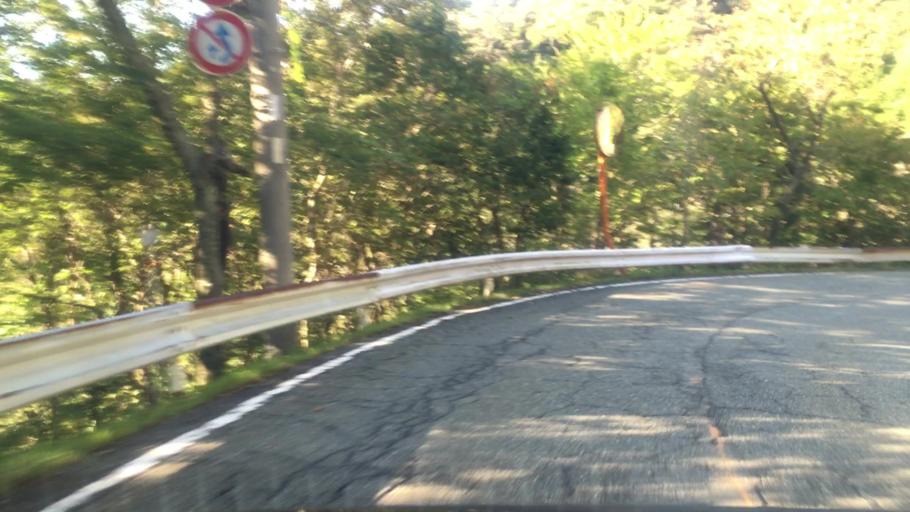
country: JP
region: Hyogo
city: Toyooka
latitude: 35.6193
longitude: 134.8713
